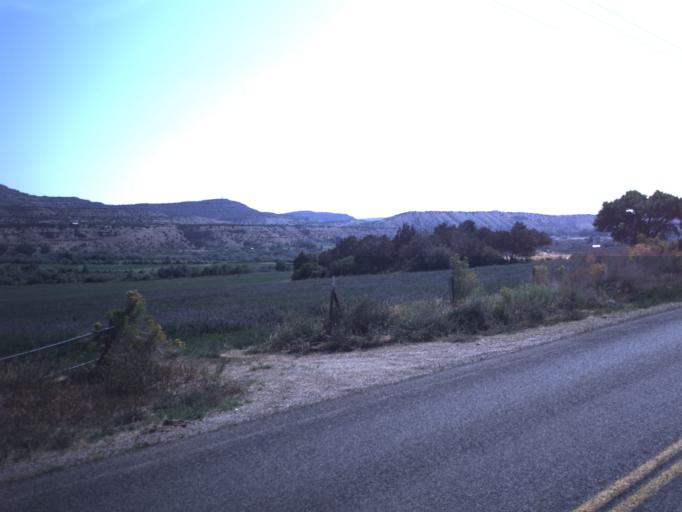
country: US
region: Utah
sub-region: Duchesne County
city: Duchesne
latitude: 40.2758
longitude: -110.4634
